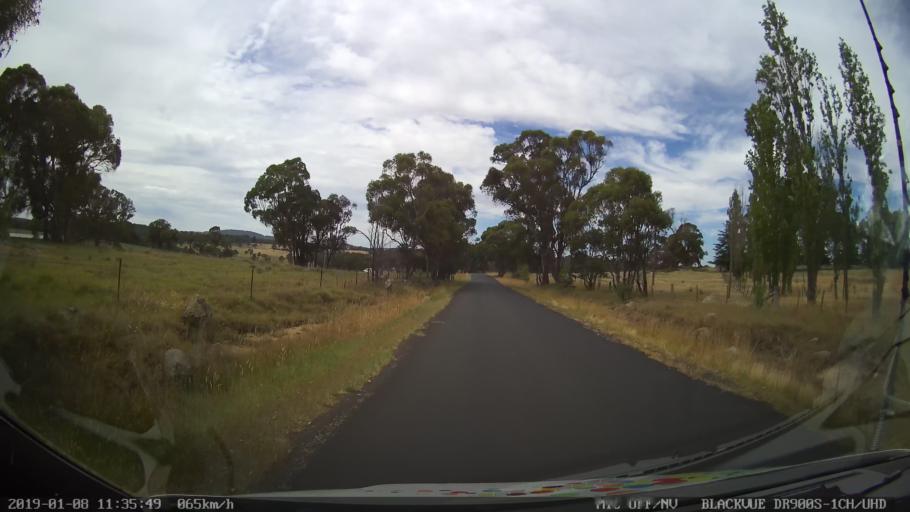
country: AU
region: New South Wales
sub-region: Guyra
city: Guyra
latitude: -30.3408
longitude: 151.5391
